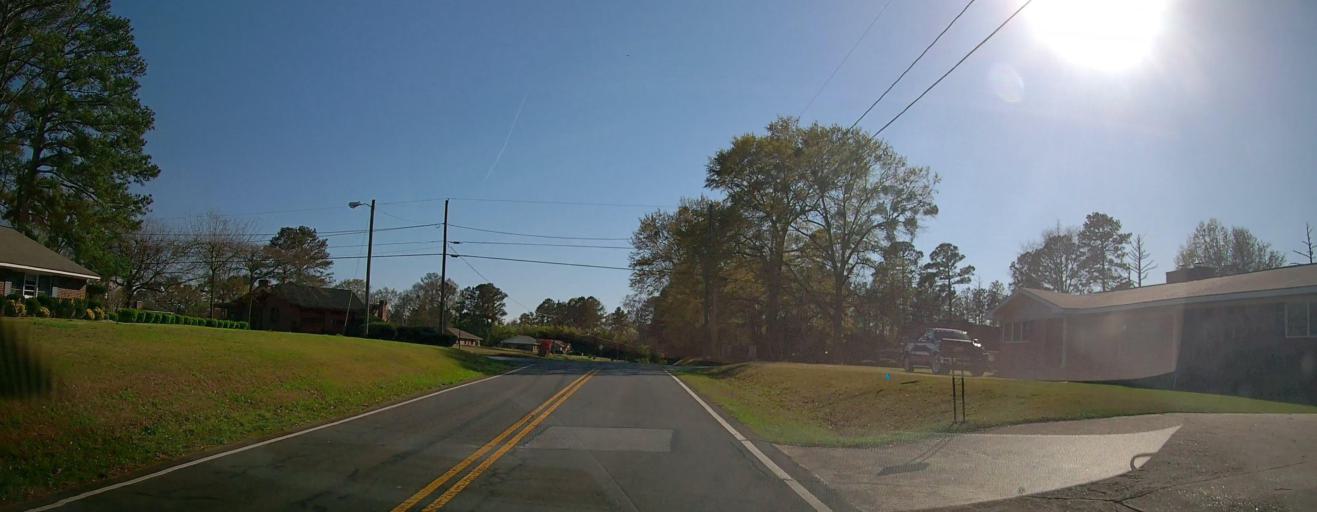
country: US
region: Georgia
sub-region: Peach County
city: Fort Valley
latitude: 32.5285
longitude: -83.9062
